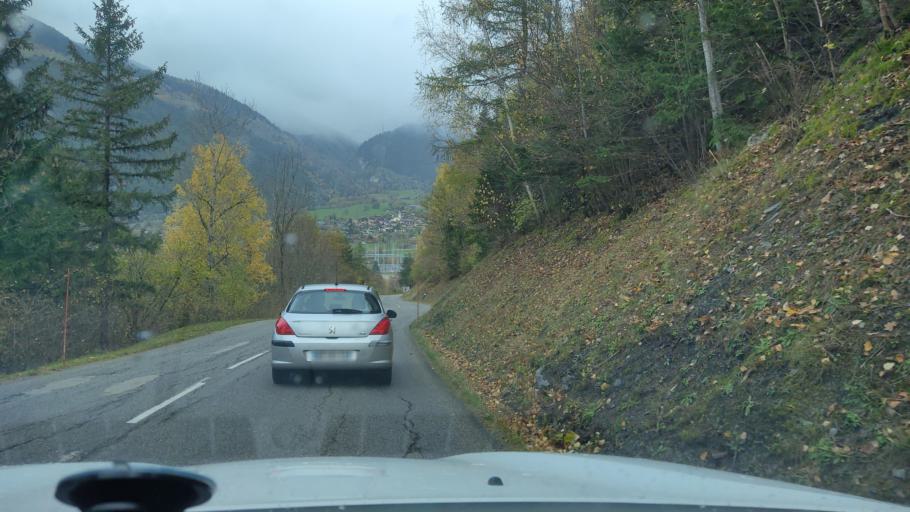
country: FR
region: Rhone-Alpes
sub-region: Departement de la Savoie
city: Bourg-Saint-Maurice
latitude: 45.6148
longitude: 6.7826
